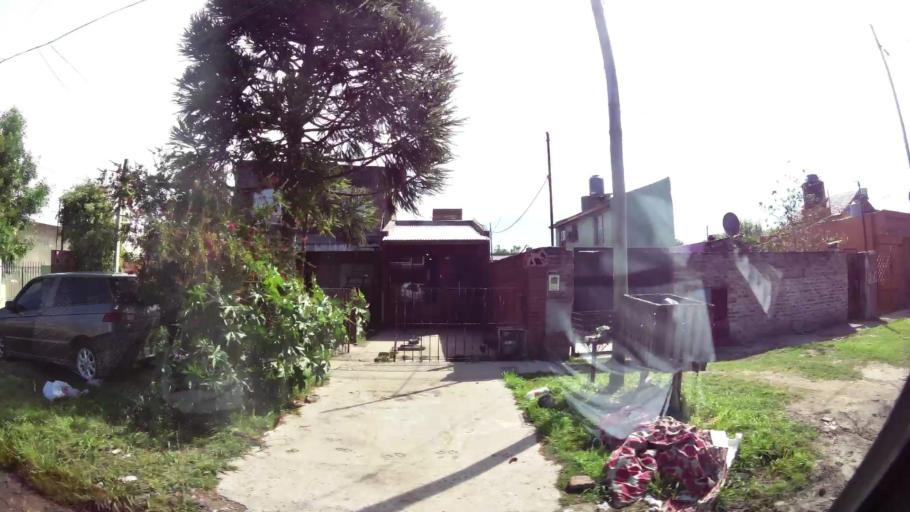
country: AR
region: Buenos Aires
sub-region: Partido de Almirante Brown
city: Adrogue
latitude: -34.8030
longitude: -58.3573
